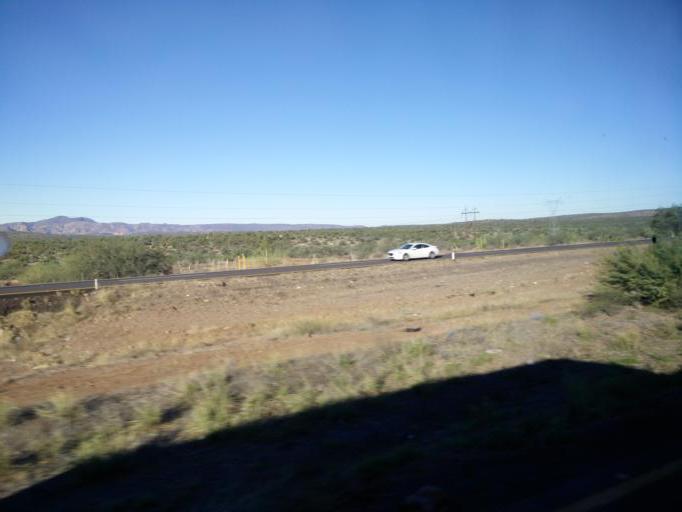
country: MX
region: Sonora
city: Heroica Guaymas
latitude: 28.2270
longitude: -111.0176
